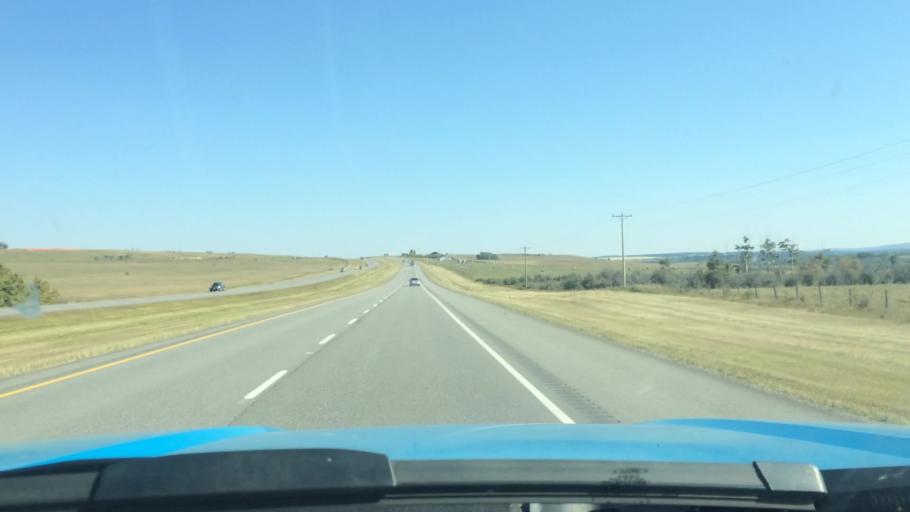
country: CA
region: Alberta
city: Cochrane
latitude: 51.0947
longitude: -114.5907
